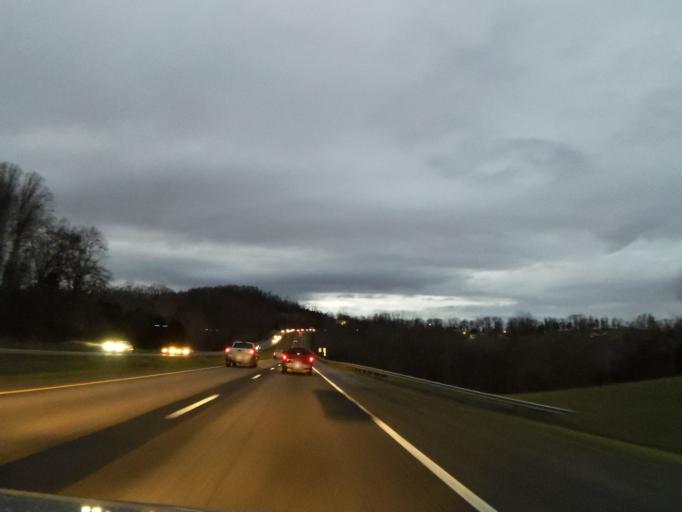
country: US
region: Tennessee
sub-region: Washington County
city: Oak Grove
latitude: 36.3852
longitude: -82.4323
